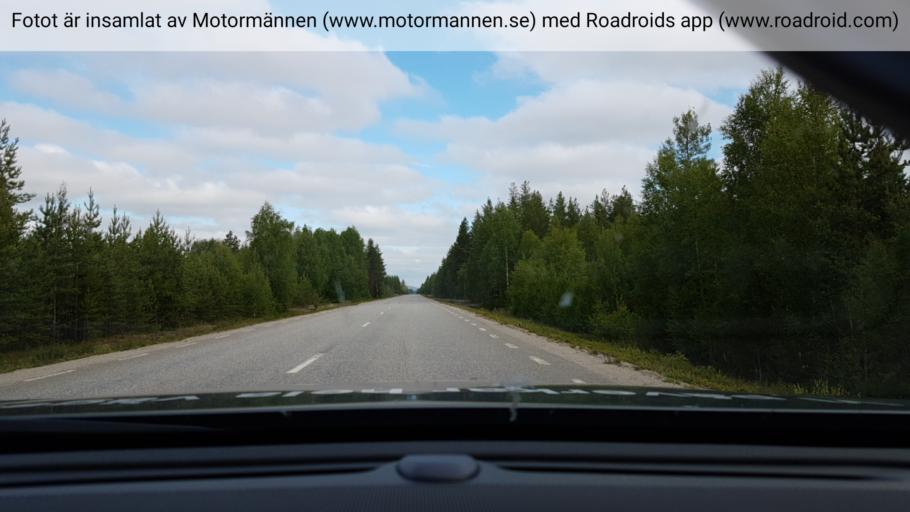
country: SE
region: Vaesterbotten
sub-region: Norsjo Kommun
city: Norsjoe
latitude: 64.5531
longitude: 19.3258
